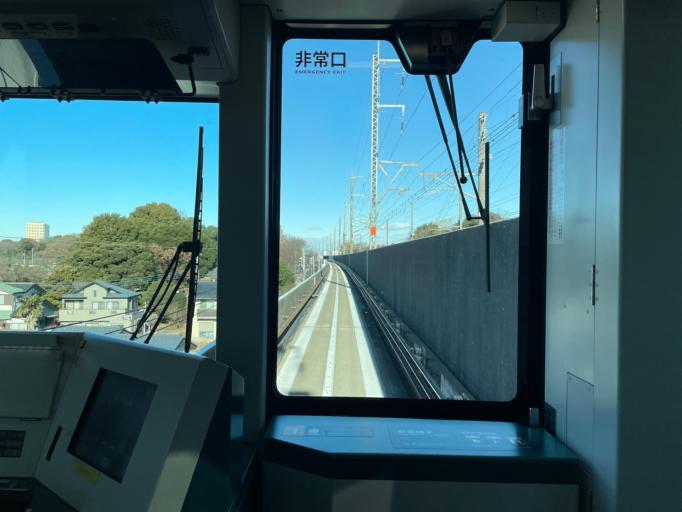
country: JP
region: Saitama
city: Ageoshimo
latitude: 35.9846
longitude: 139.6242
